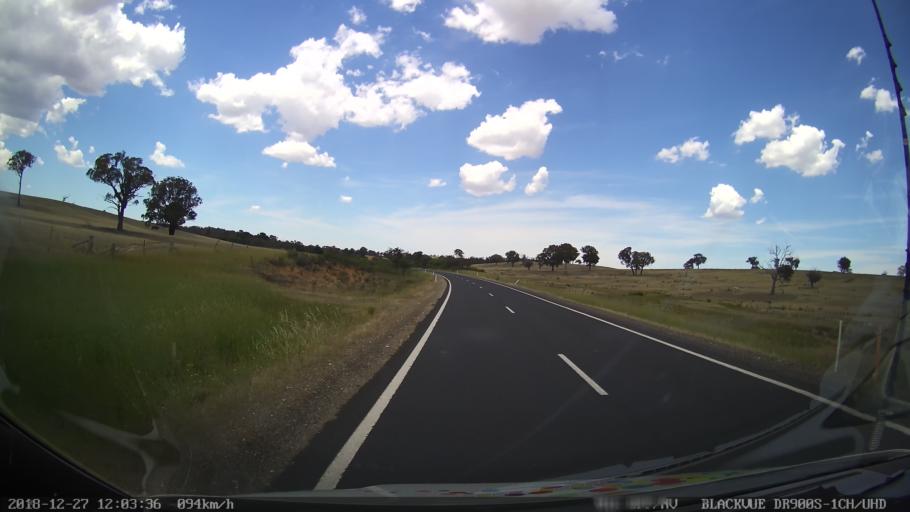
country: AU
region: New South Wales
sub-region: Blayney
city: Blayney
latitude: -33.7873
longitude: 149.3576
